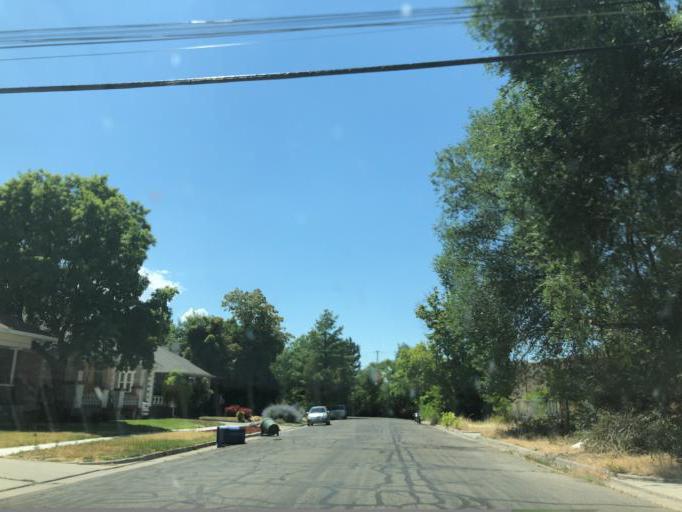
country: US
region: Utah
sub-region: Salt Lake County
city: South Salt Lake
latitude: 40.7185
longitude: -111.8686
